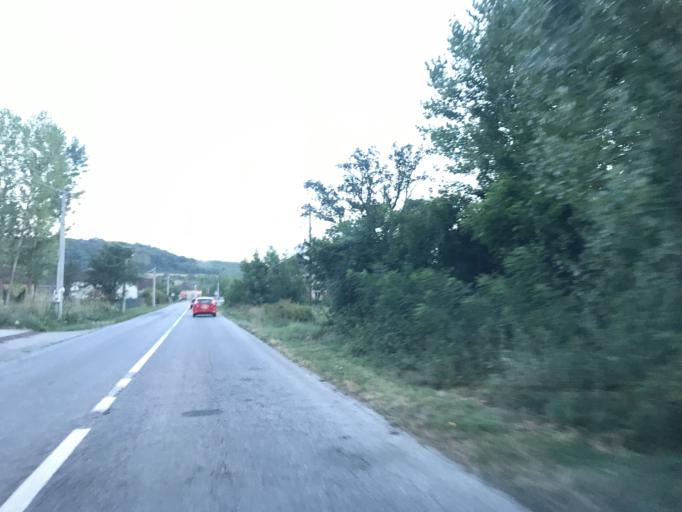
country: RS
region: Central Serbia
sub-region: Branicevski Okrug
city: Veliko Gradiste
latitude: 44.7137
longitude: 21.3957
